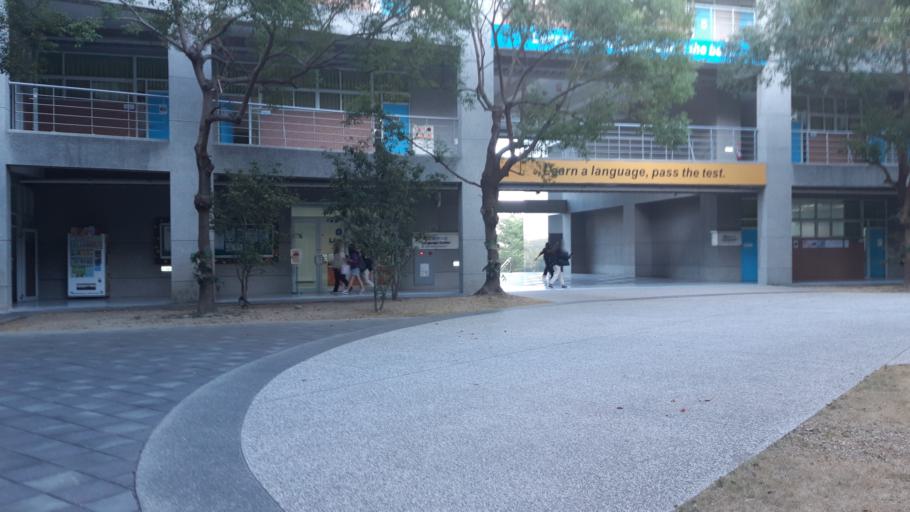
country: TW
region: Taiwan
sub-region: Changhua
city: Chang-hua
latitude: 24.1345
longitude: 120.6023
